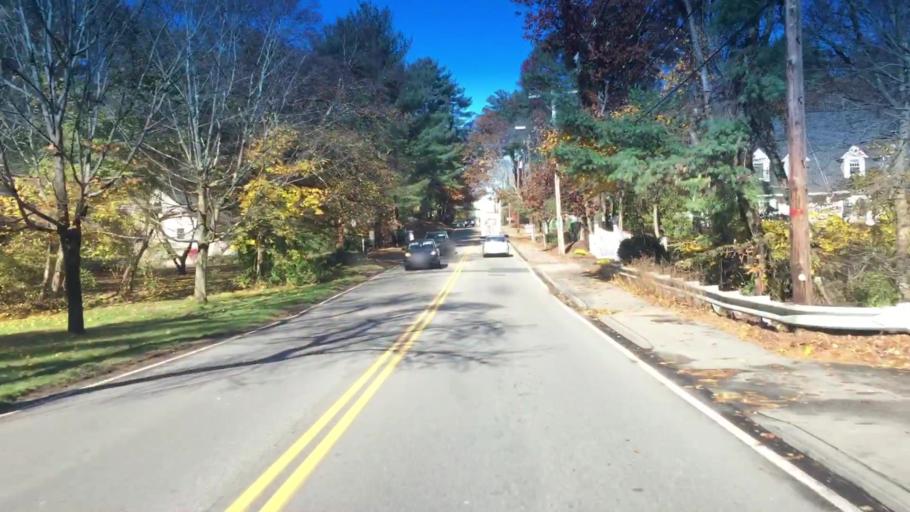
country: US
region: Massachusetts
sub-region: Norfolk County
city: Medfield
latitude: 42.1815
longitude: -71.3048
